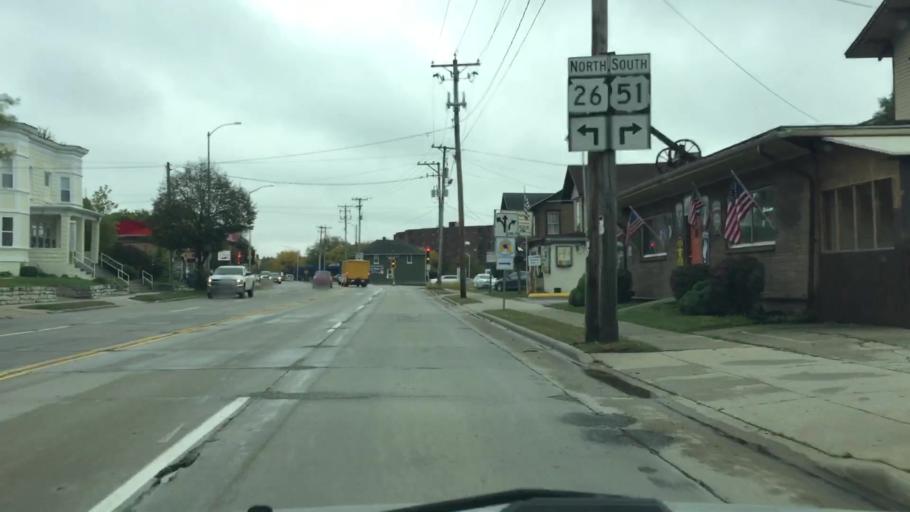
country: US
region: Wisconsin
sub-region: Rock County
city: Janesville
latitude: 42.6872
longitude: -89.0256
